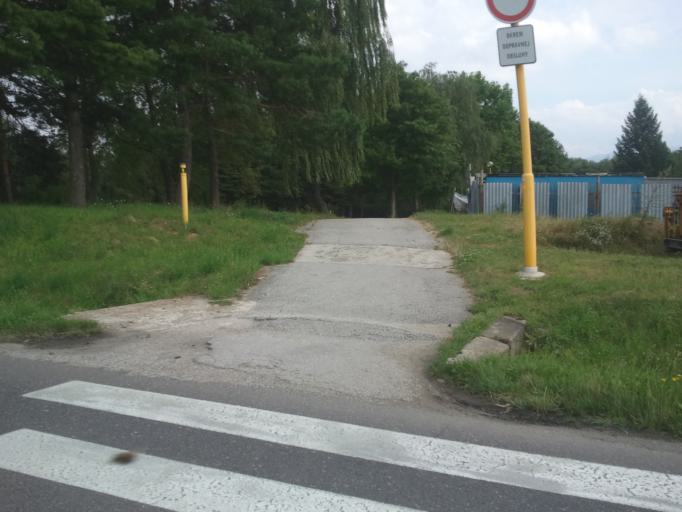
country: SK
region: Nitriansky
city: Bojnice
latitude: 48.7769
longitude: 18.5919
